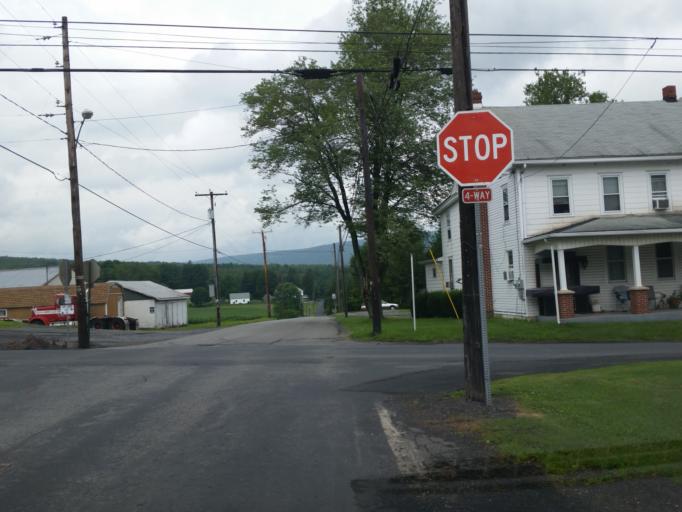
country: US
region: Pennsylvania
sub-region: Schuylkill County
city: Tower City
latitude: 40.5708
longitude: -76.5473
